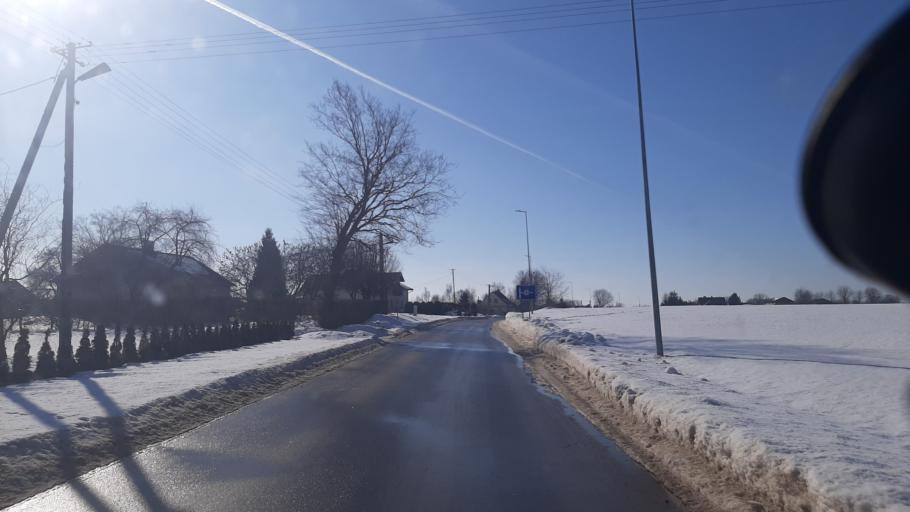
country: PL
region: Lublin Voivodeship
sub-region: Powiat lubelski
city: Garbow
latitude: 51.2977
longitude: 22.3047
